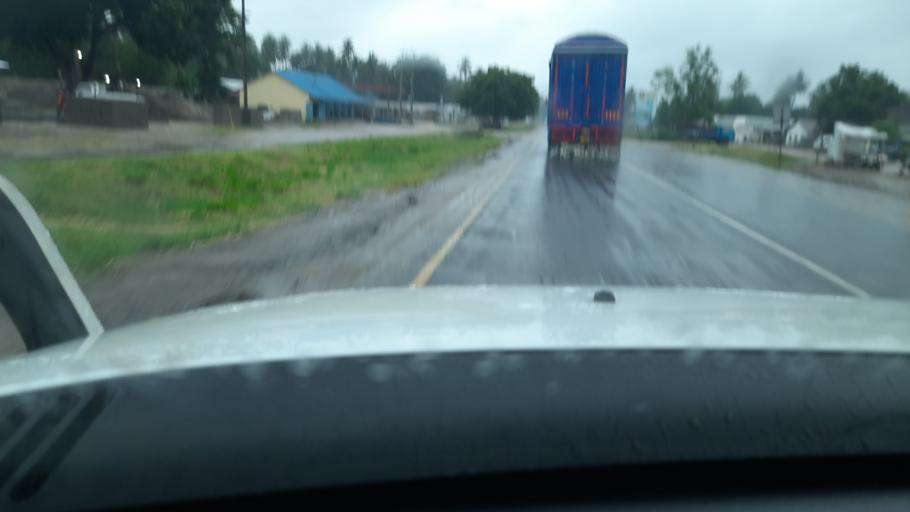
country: TZ
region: Pwani
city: Bagamoyo
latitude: -6.5903
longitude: 39.0584
